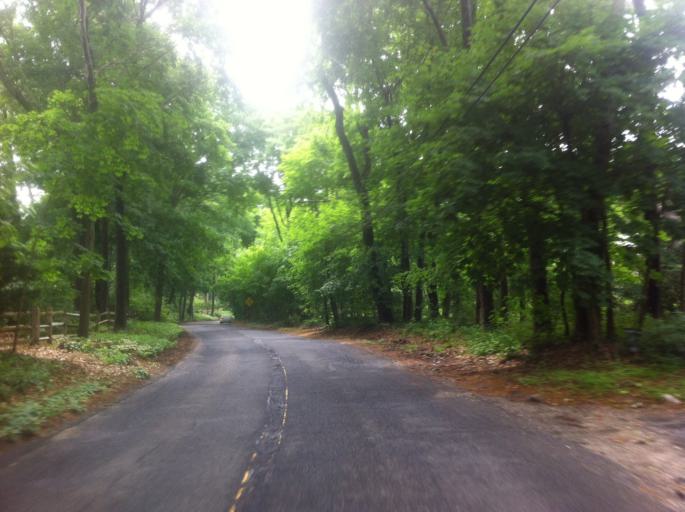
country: US
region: New York
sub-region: Nassau County
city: Upper Brookville
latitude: 40.8386
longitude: -73.5509
